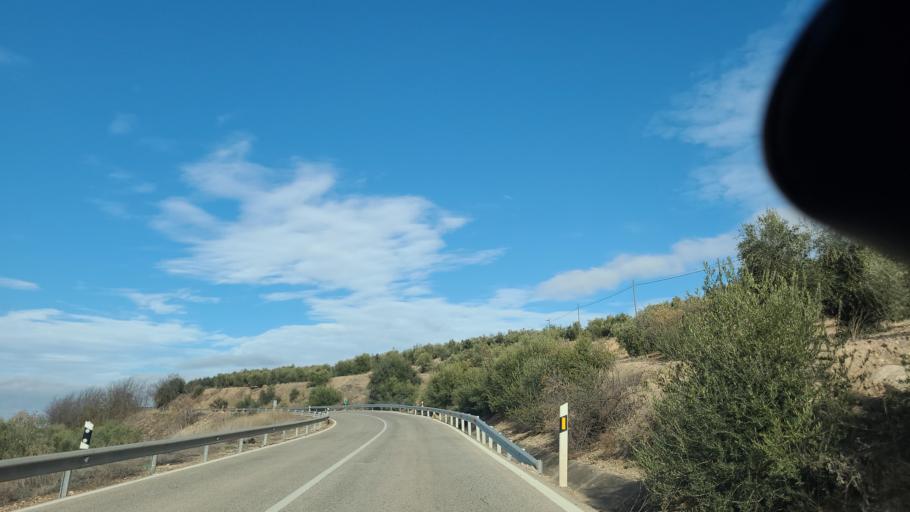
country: ES
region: Andalusia
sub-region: Provincia de Jaen
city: Espeluy
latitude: 38.0200
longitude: -3.8809
